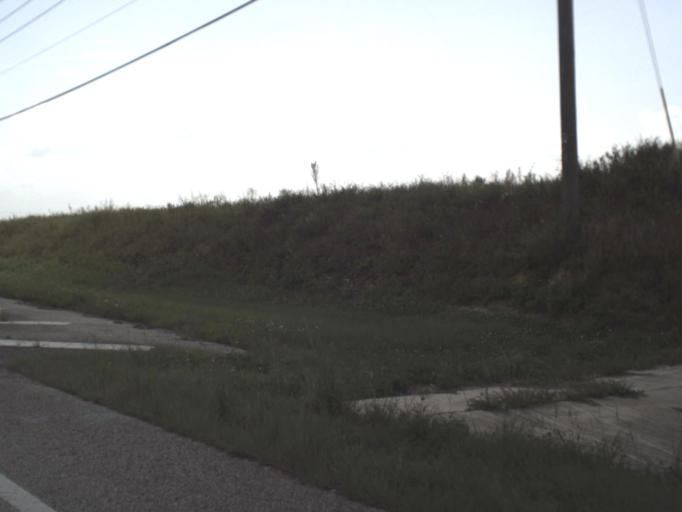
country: US
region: Florida
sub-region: Polk County
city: Davenport
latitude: 28.2030
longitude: -81.6400
